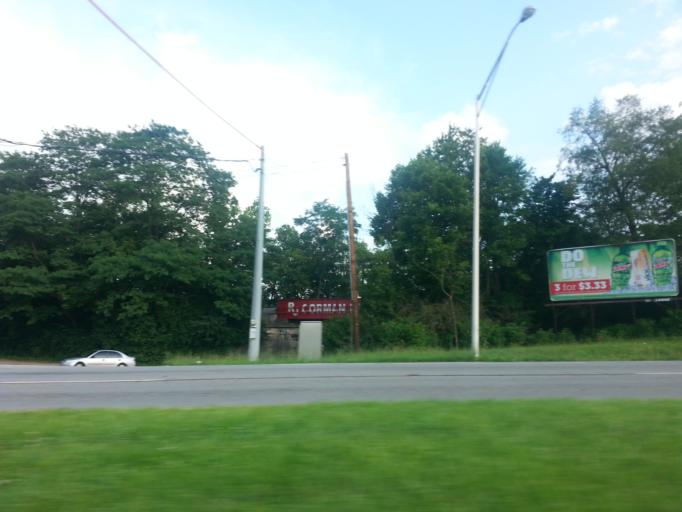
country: US
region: Kentucky
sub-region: Fayette County
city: Lexington-Fayette
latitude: 38.0786
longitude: -84.4508
